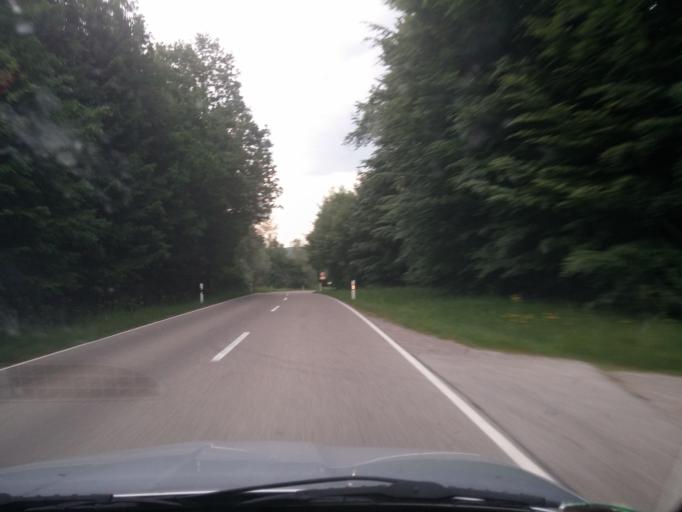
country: DE
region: Bavaria
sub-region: Swabia
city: Legau
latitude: 47.8445
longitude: 10.1201
